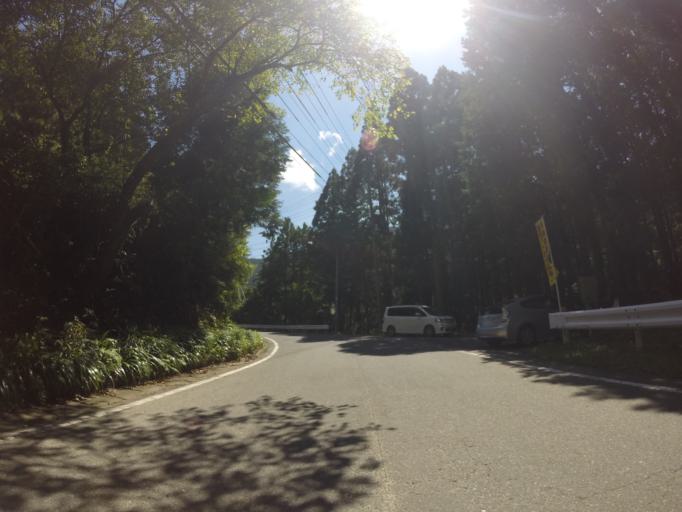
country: JP
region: Shizuoka
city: Shizuoka-shi
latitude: 35.0603
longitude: 138.2444
